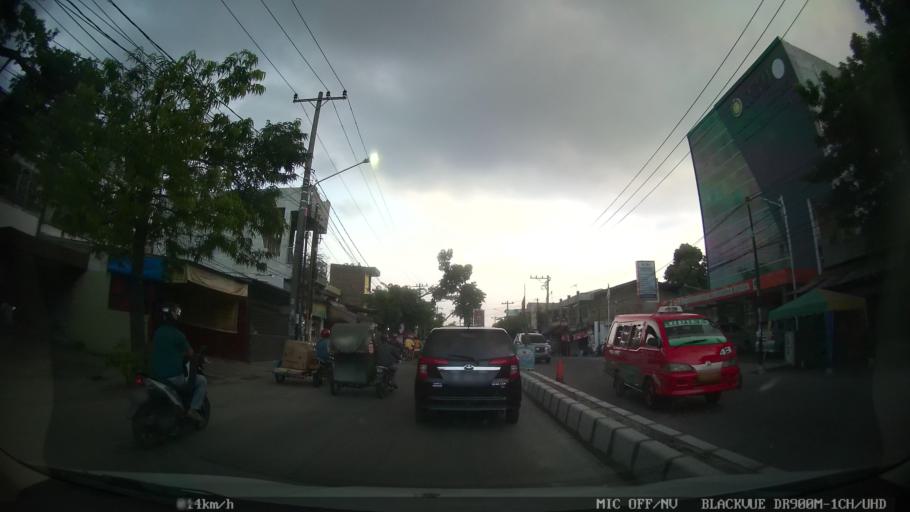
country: ID
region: North Sumatra
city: Medan
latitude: 3.5834
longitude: 98.7112
